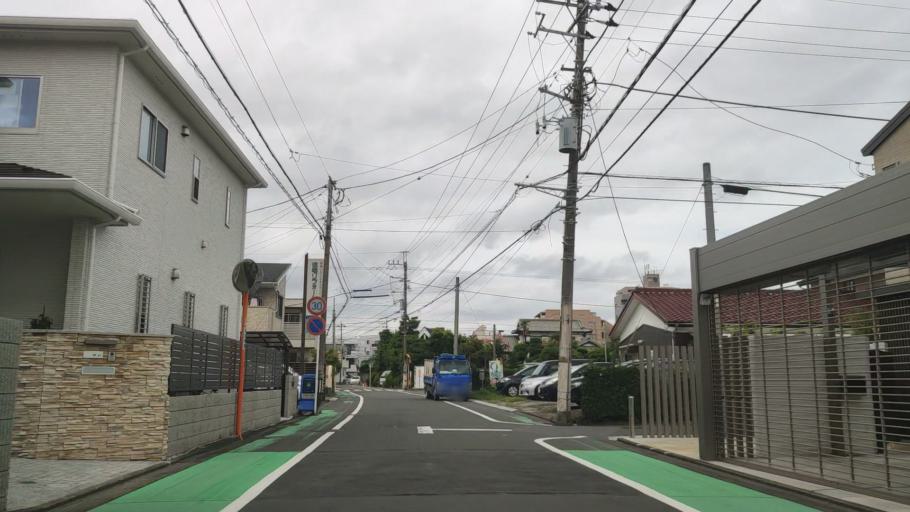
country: JP
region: Tokyo
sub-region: Machida-shi
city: Machida
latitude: 35.5174
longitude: 139.4352
